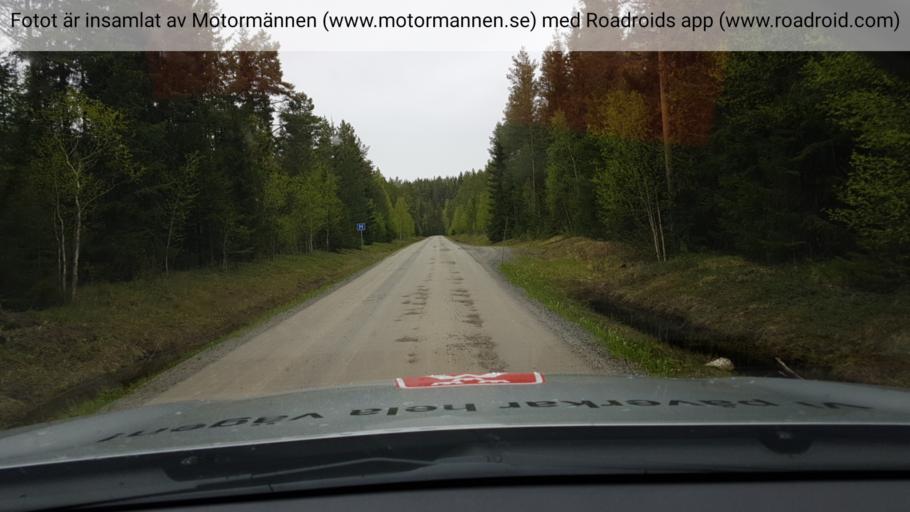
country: SE
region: Jaemtland
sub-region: OEstersunds Kommun
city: Brunflo
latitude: 62.9415
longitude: 14.6658
